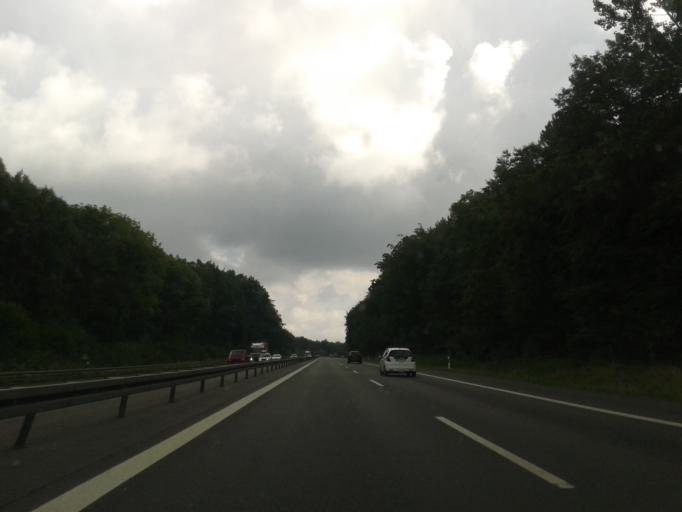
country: DE
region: Saxony
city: Grossrohrsdorf
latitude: 51.1567
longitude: 14.0172
